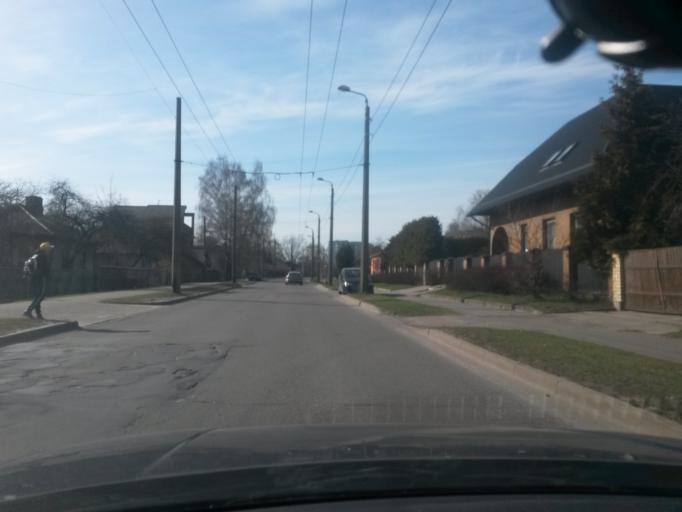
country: LV
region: Kekava
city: Kekava
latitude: 56.9058
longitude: 24.2034
